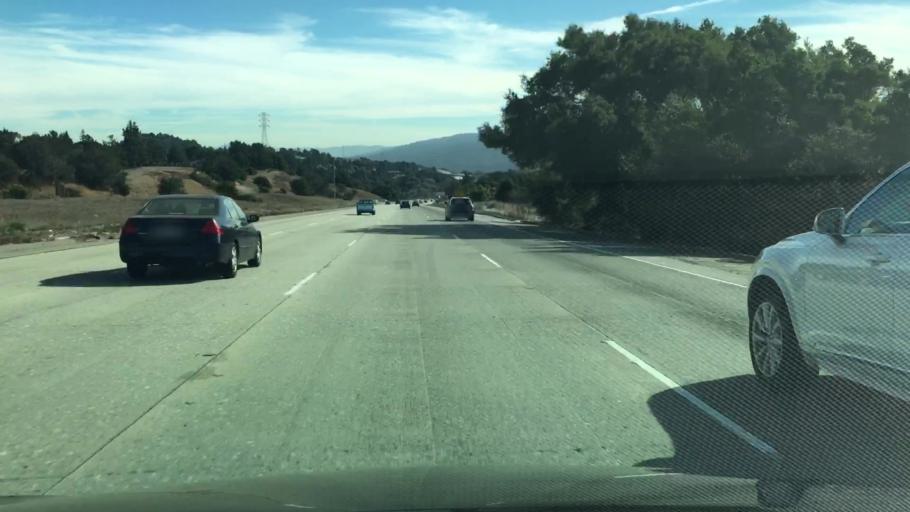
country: US
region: California
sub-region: San Mateo County
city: Highlands-Baywood Park
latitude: 37.5364
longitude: -122.3659
